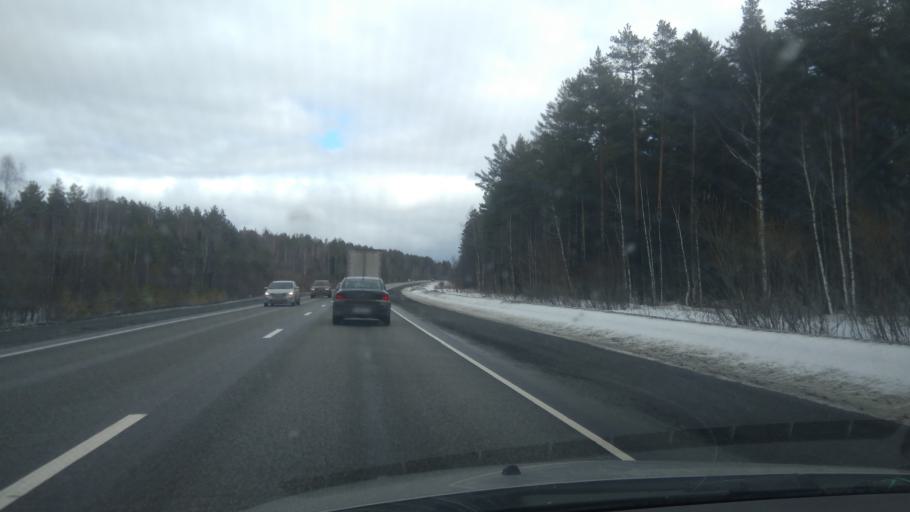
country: RU
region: Sverdlovsk
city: Bisert'
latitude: 56.8299
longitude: 58.7771
